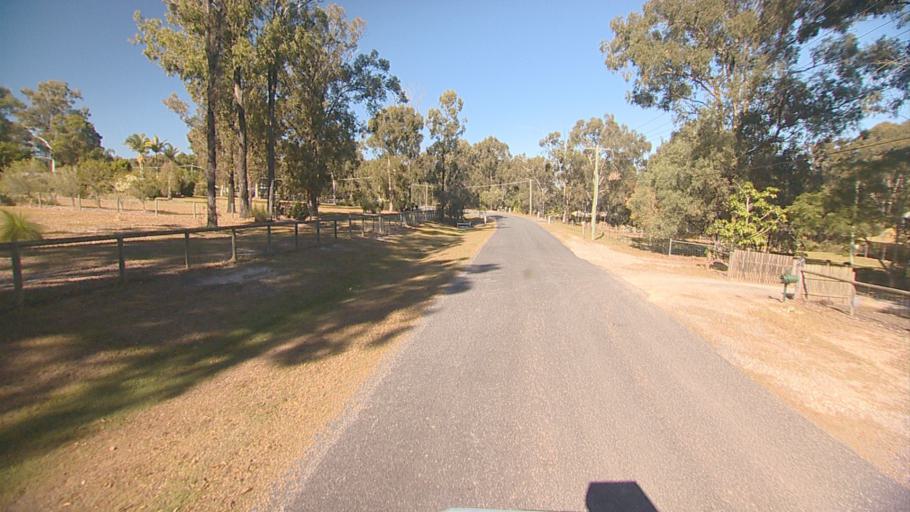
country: AU
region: Queensland
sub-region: Logan
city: Chambers Flat
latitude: -27.7907
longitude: 153.1290
